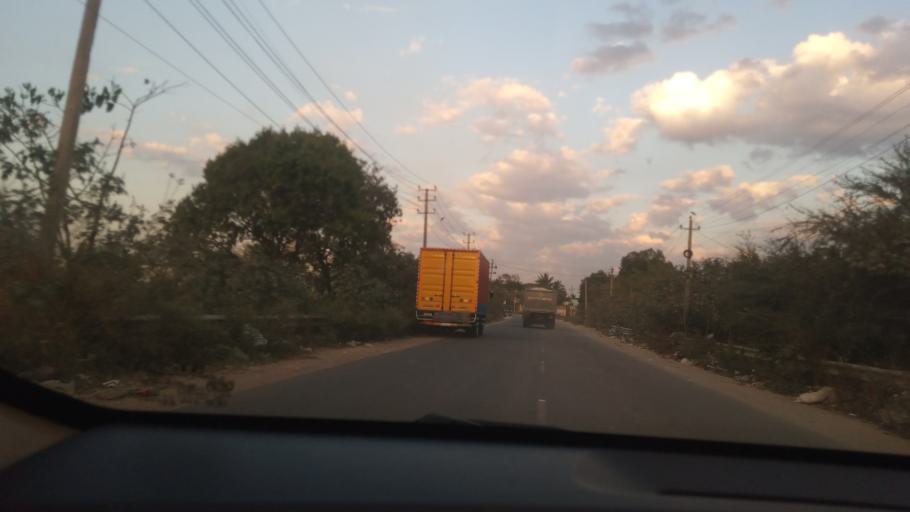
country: IN
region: Karnataka
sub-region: Bangalore Rural
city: Hoskote
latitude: 12.9798
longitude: 77.7973
